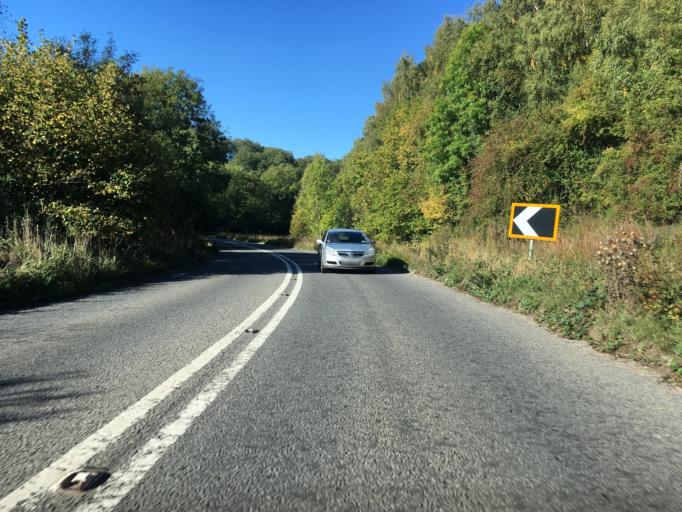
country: GB
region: England
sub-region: Wiltshire
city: Biddestone
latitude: 51.4712
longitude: -2.2143
